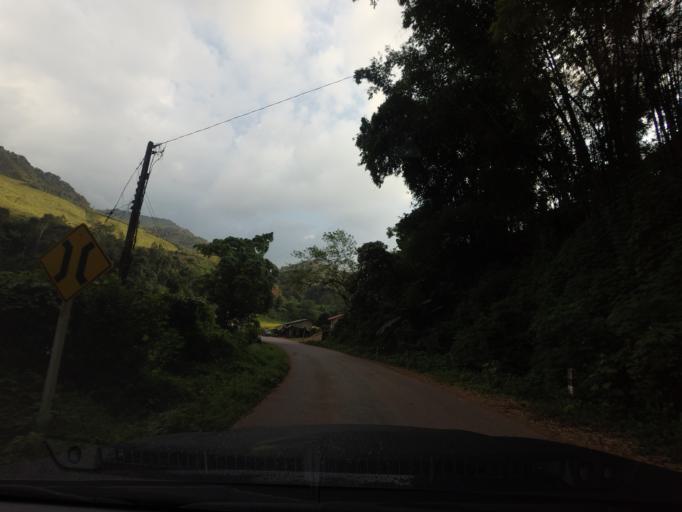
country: TH
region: Nan
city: Bo Kluea
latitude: 19.2713
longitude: 101.1779
